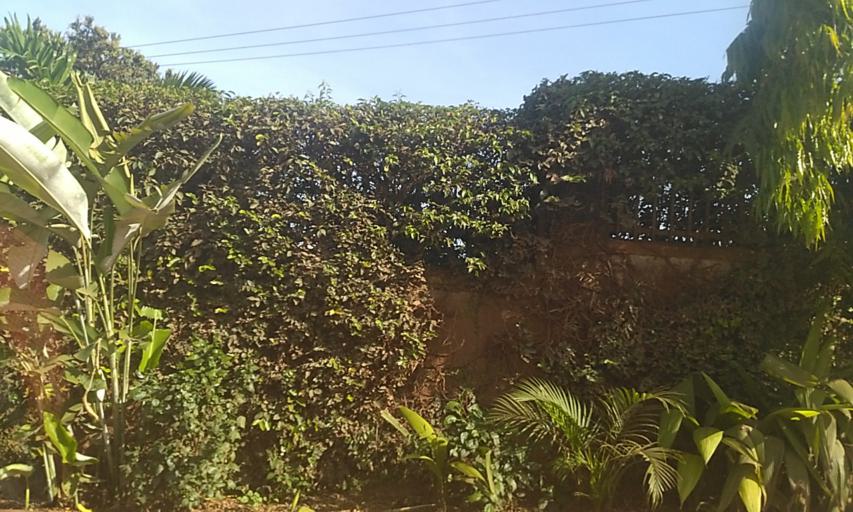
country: UG
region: Central Region
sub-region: Wakiso District
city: Kireka
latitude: 0.3606
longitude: 32.6185
